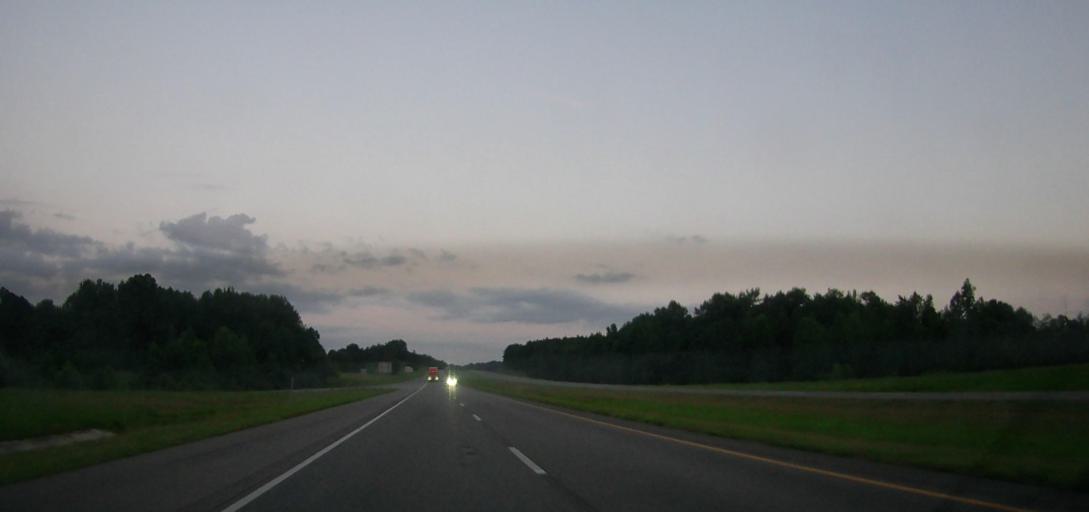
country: US
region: Alabama
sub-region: Marion County
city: Hamilton
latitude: 34.1649
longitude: -88.0632
